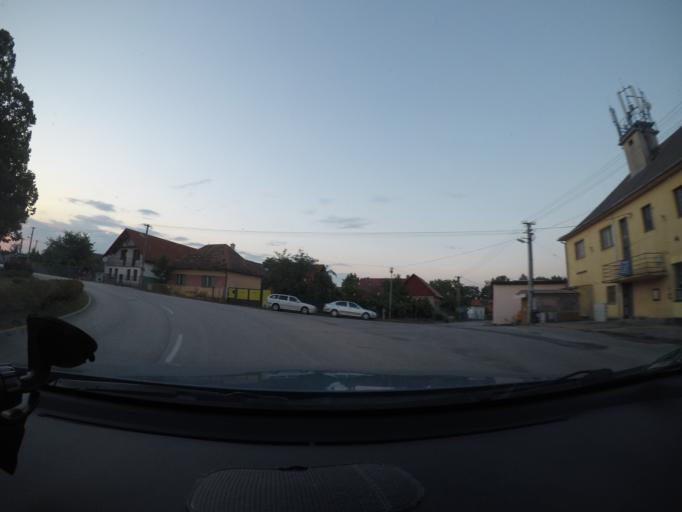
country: SK
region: Trenciansky
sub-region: Okres Trencin
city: Trencin
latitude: 48.8664
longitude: 17.9451
